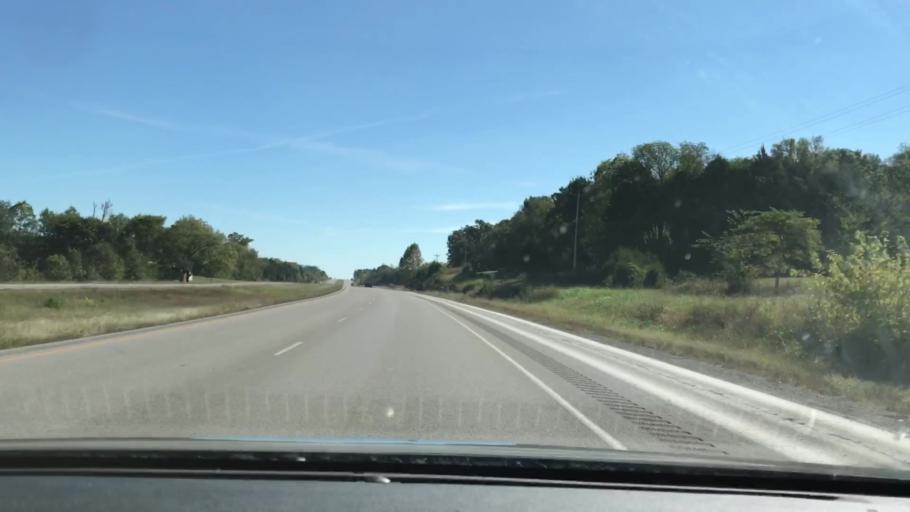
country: US
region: Kentucky
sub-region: Christian County
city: Hopkinsville
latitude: 36.8478
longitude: -87.3316
